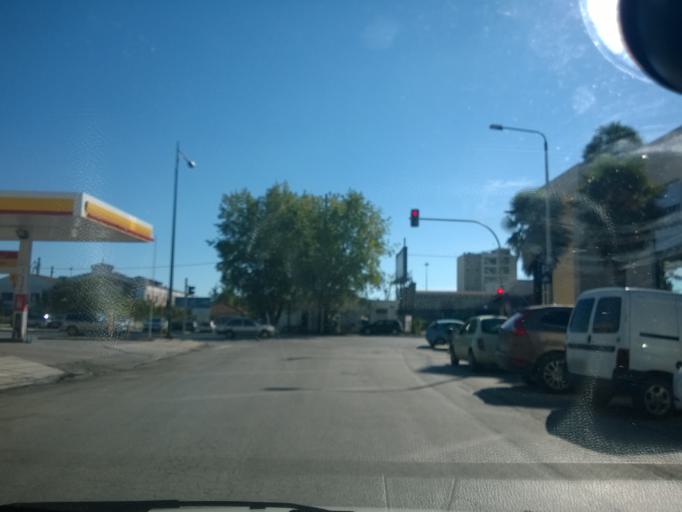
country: GR
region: Central Macedonia
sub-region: Nomos Thessalonikis
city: Ampelokipoi
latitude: 40.6432
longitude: 22.9124
